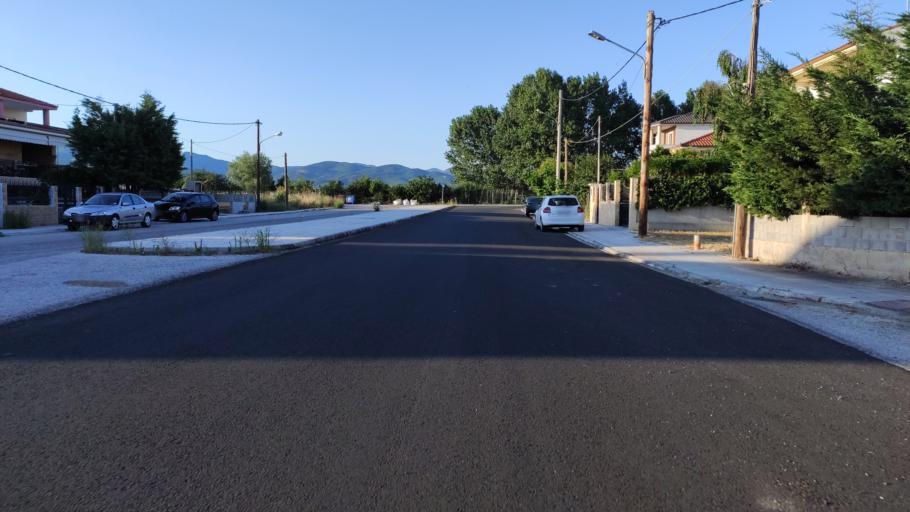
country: GR
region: East Macedonia and Thrace
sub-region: Nomos Rodopis
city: Komotini
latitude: 41.1318
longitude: 25.3977
